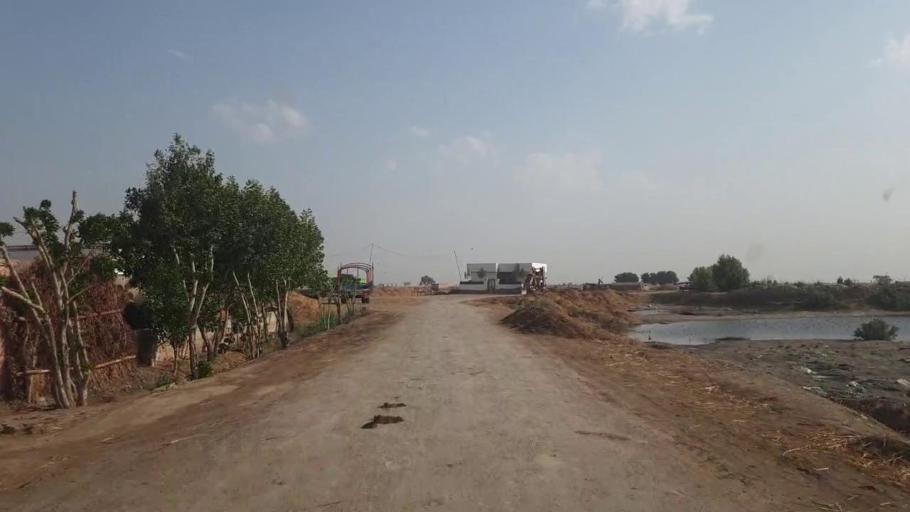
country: PK
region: Sindh
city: Kario
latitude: 24.5801
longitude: 68.5416
